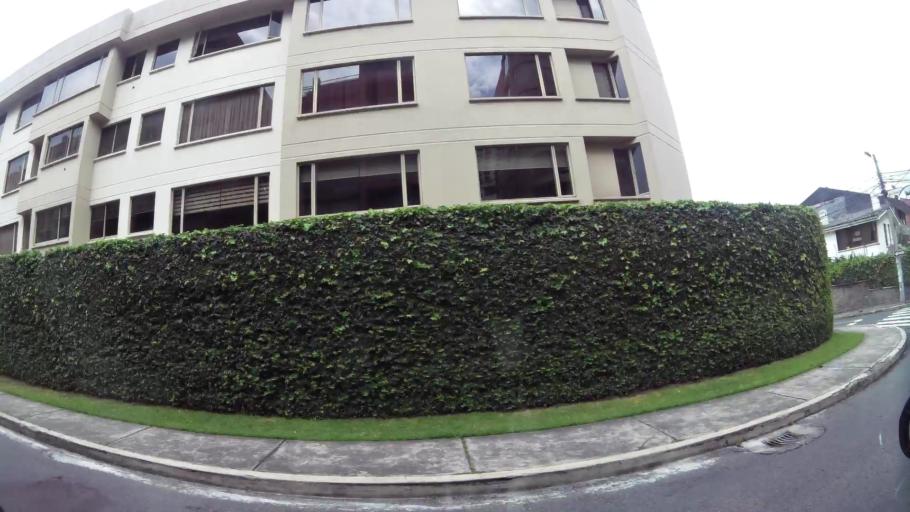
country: EC
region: Pichincha
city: Quito
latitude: -0.1676
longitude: -78.4958
